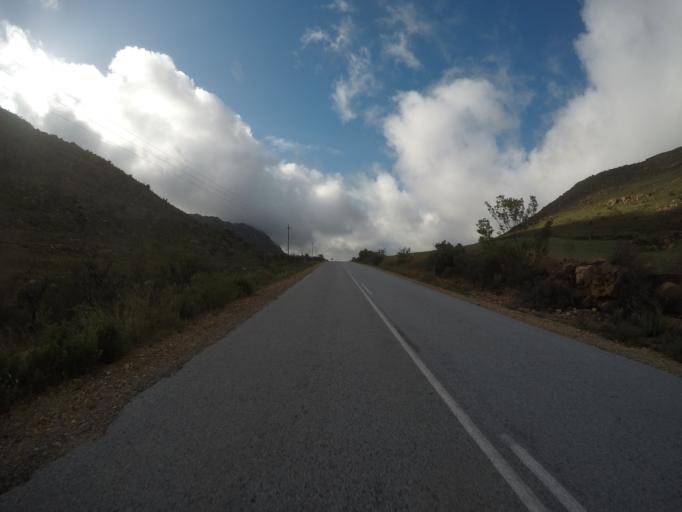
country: ZA
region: Western Cape
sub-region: West Coast District Municipality
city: Clanwilliam
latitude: -32.3708
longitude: 18.8661
